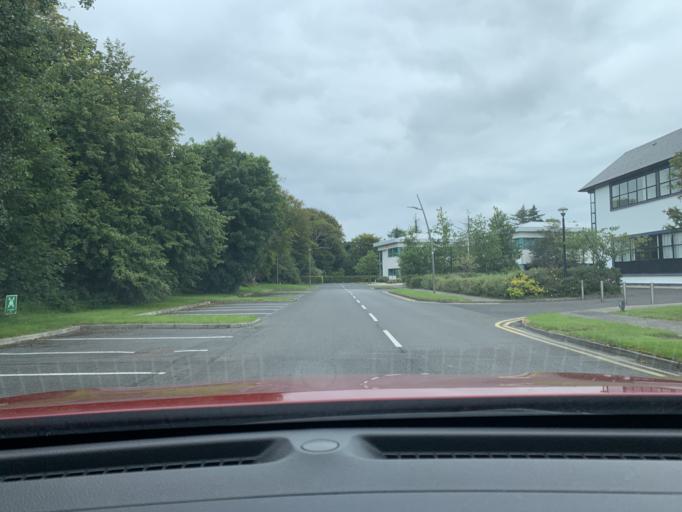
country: IE
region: Connaught
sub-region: Sligo
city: Sligo
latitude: 54.2739
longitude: -8.4991
